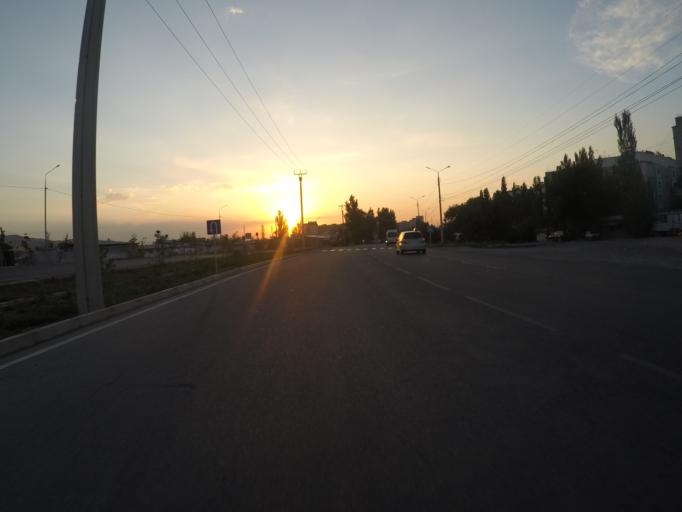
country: KG
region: Chuy
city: Bishkek
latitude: 42.8110
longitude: 74.6352
